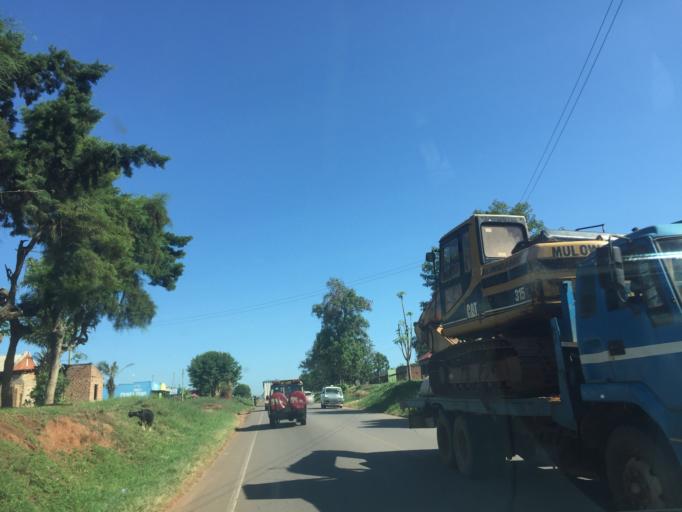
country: UG
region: Central Region
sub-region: Luwero District
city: Wobulenzi
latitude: 0.7623
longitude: 32.5132
